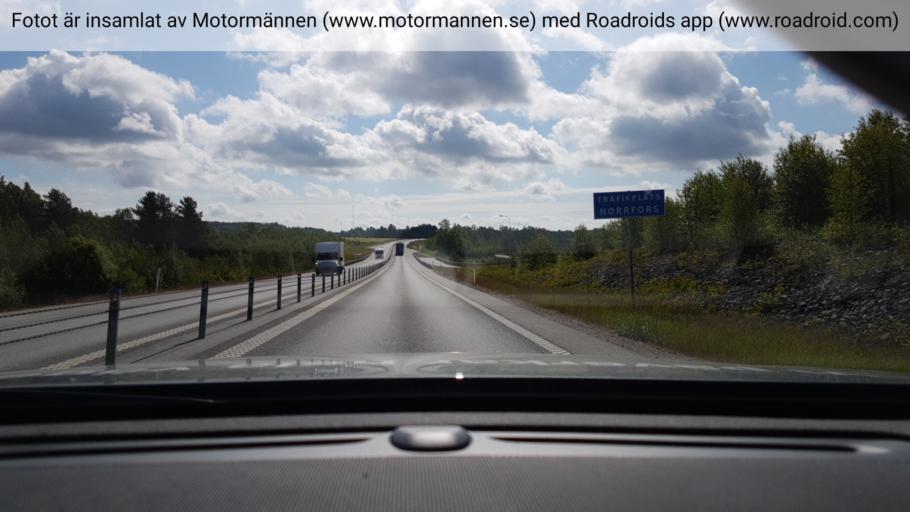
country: SE
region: Vaesterbotten
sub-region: Umea Kommun
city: Roback
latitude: 63.8856
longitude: 20.0279
